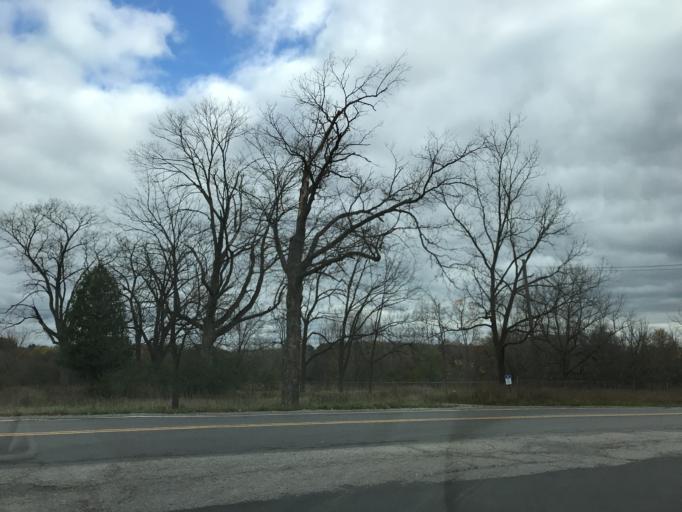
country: US
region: Michigan
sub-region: Washtenaw County
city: Ann Arbor
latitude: 42.2882
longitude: -83.6715
